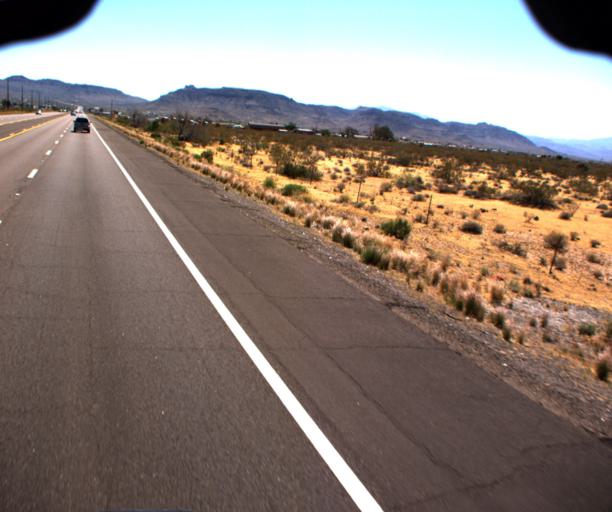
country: US
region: Arizona
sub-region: Mohave County
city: Golden Valley
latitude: 35.2208
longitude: -114.1919
